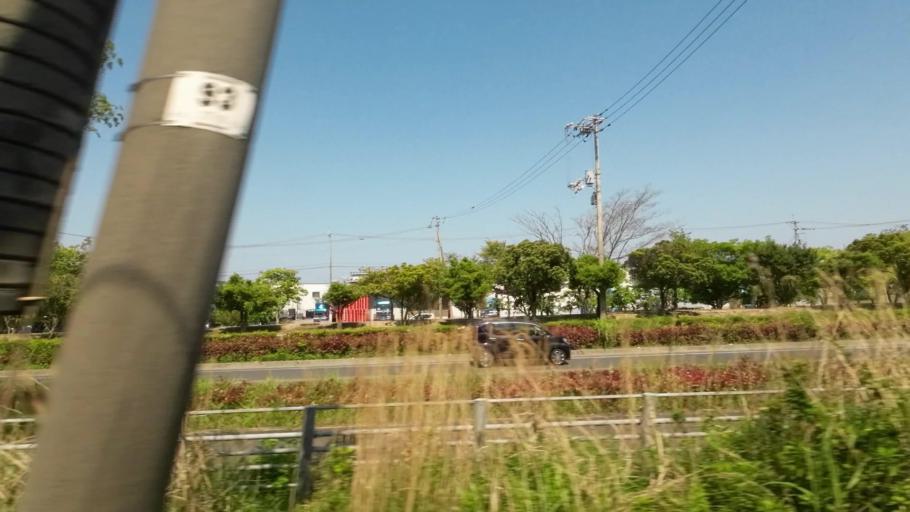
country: JP
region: Ehime
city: Kawanoecho
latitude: 34.0281
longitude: 133.5831
